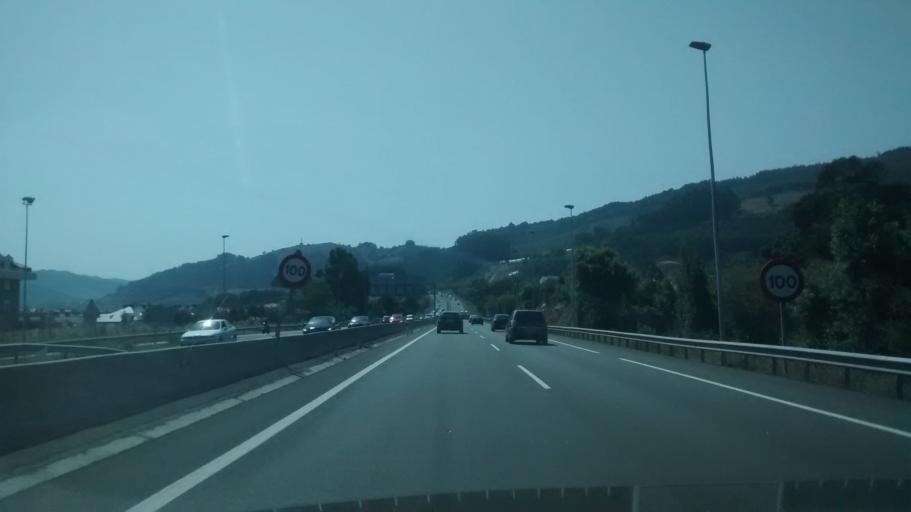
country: ES
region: Cantabria
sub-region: Provincia de Cantabria
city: Castro-Urdiales
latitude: 43.3917
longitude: -3.2347
